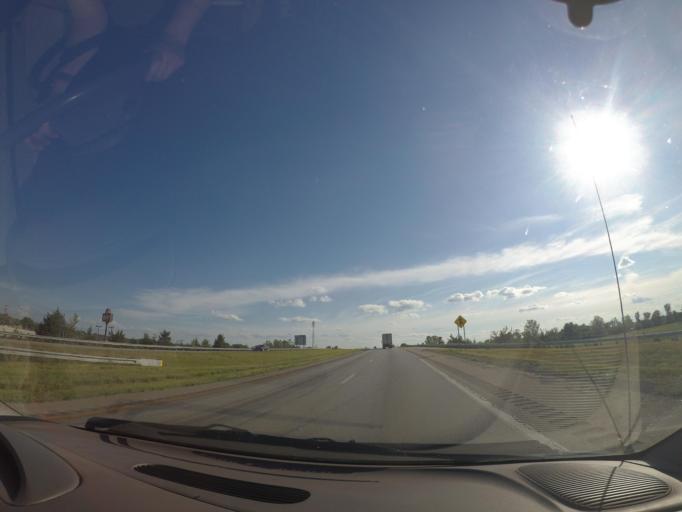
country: US
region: Ohio
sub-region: Henry County
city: Napoleon
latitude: 41.4080
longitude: -84.1330
